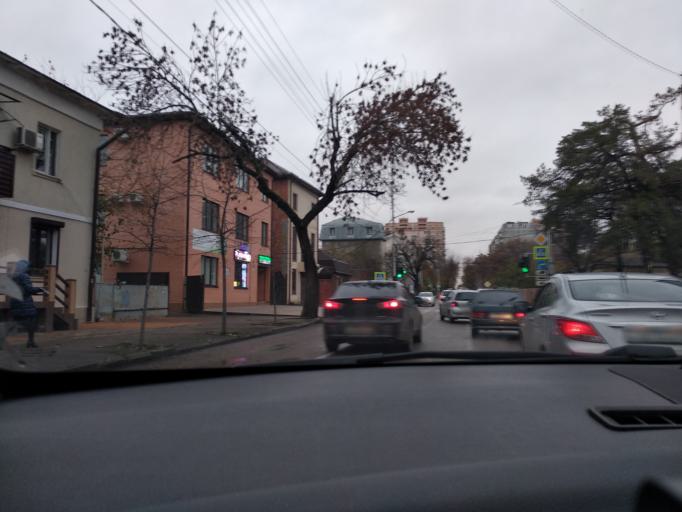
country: RU
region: Krasnodarskiy
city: Krasnodar
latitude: 45.0220
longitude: 38.9812
